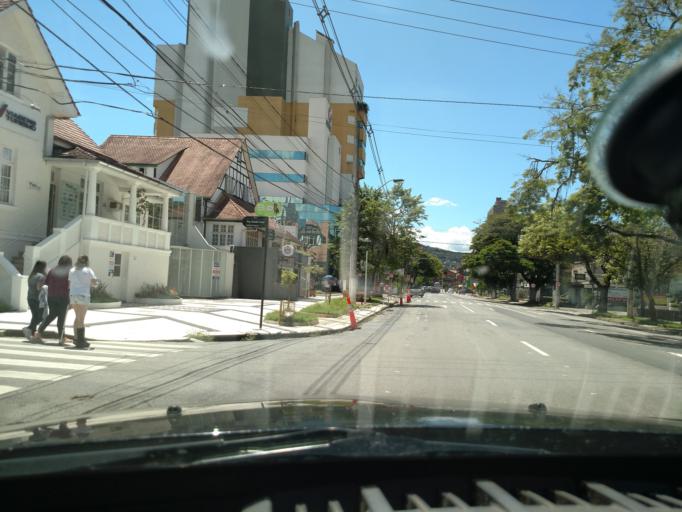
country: BR
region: Santa Catarina
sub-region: Blumenau
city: Blumenau
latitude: -26.9254
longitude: -49.0613
